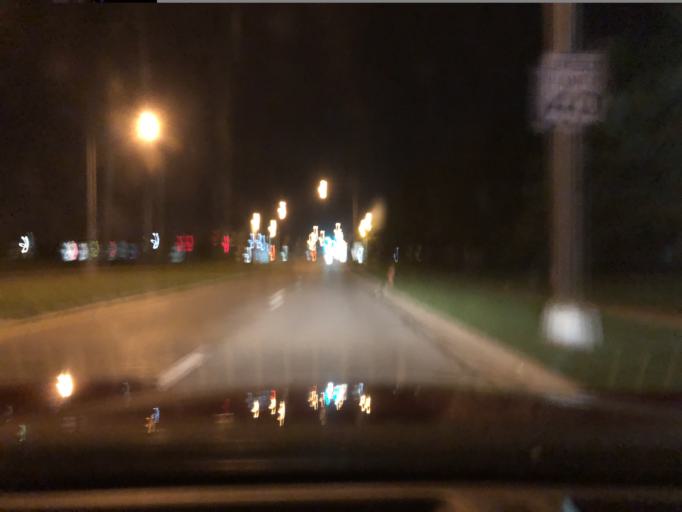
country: US
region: Ohio
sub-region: Franklin County
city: Dublin
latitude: 40.0648
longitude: -83.0921
